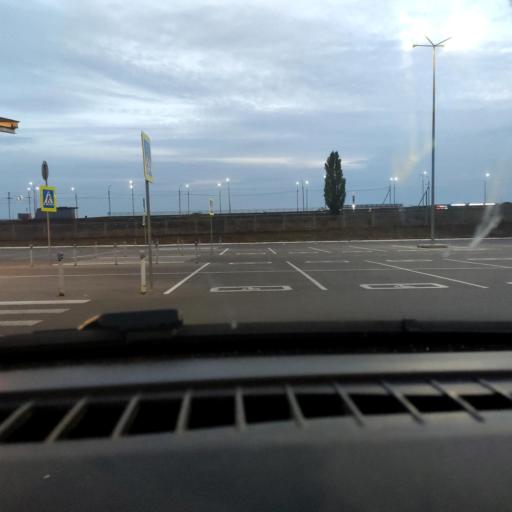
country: RU
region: Voronezj
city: Pridonskoy
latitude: 51.6529
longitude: 39.0613
